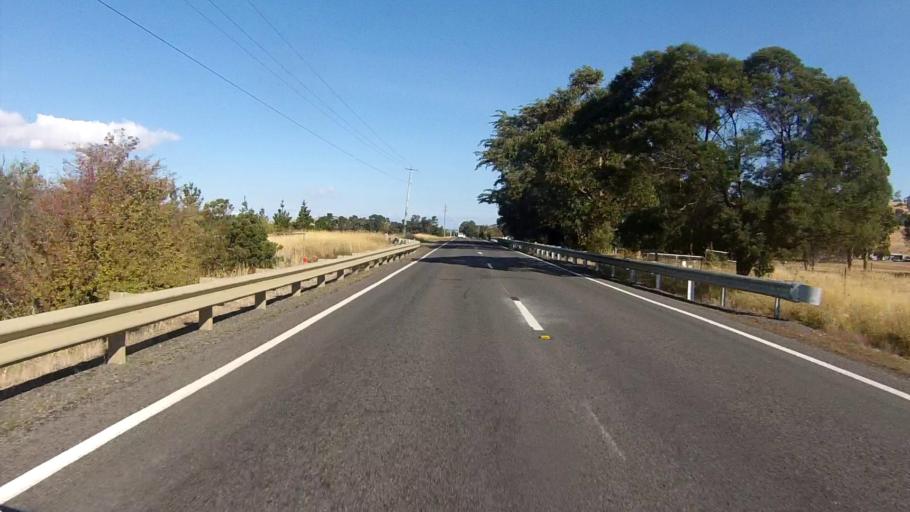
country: AU
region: Tasmania
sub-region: Sorell
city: Sorell
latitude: -42.7238
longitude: 147.5215
